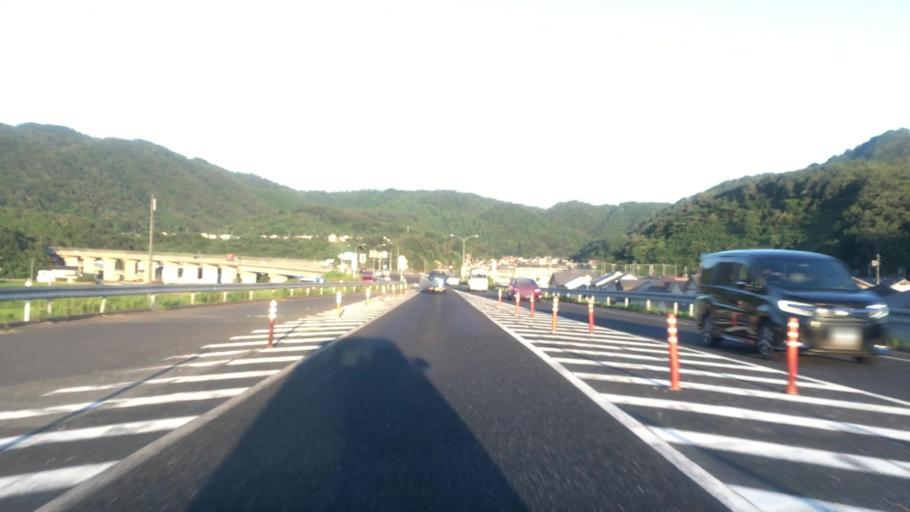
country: JP
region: Tottori
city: Tottori
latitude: 35.5224
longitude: 134.2299
